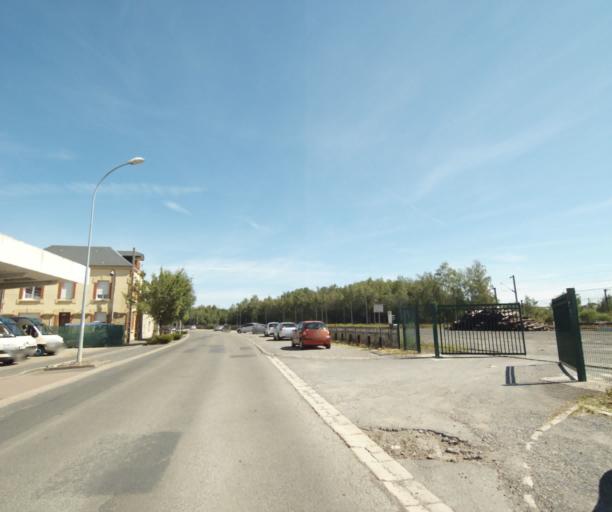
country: FR
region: Champagne-Ardenne
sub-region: Departement des Ardennes
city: Villers-Semeuse
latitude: 49.7466
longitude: 4.7359
